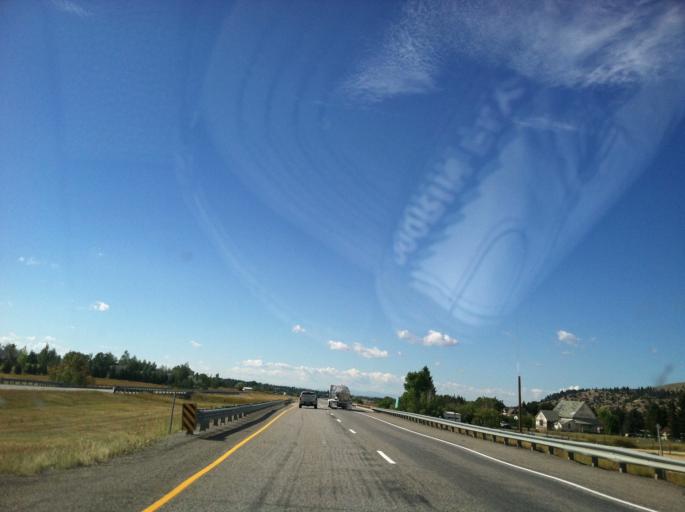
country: US
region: Montana
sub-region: Gallatin County
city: Bozeman
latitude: 45.6662
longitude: -110.9799
